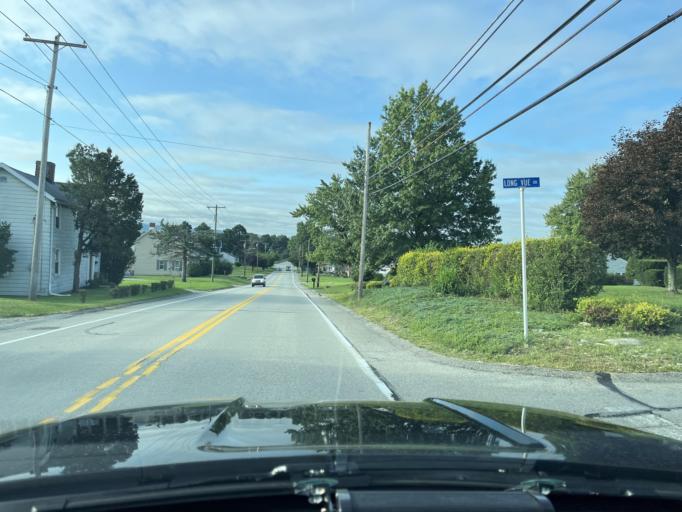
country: US
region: Pennsylvania
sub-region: Fayette County
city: Leith-Hatfield
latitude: 39.8740
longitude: -79.7411
